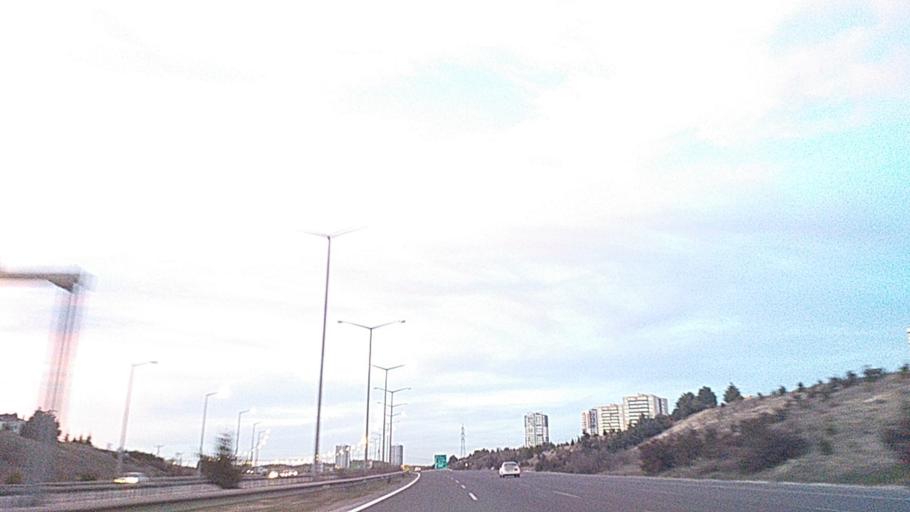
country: TR
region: Ankara
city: Etimesgut
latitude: 39.9973
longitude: 32.6371
